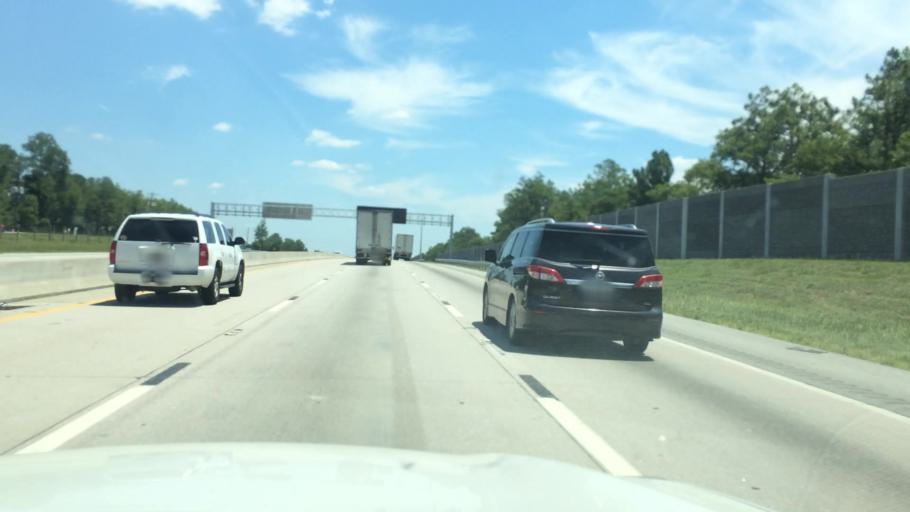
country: US
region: South Carolina
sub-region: Richland County
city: Woodfield
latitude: 34.0785
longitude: -80.8959
